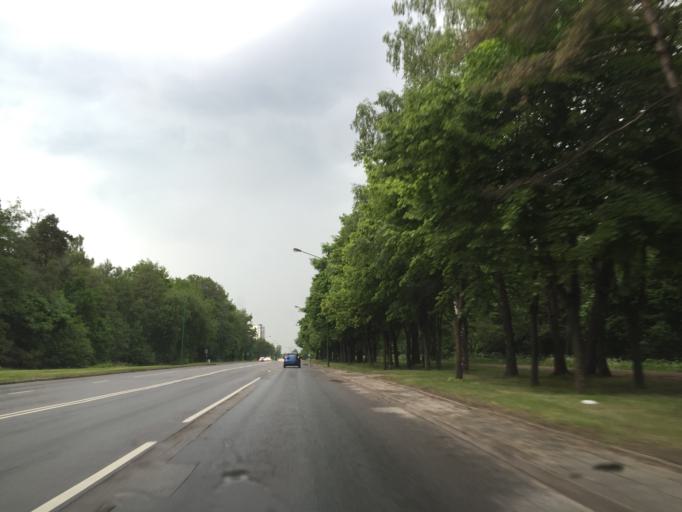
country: LT
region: Klaipedos apskritis
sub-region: Klaipeda
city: Klaipeda
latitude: 55.7396
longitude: 21.1300
